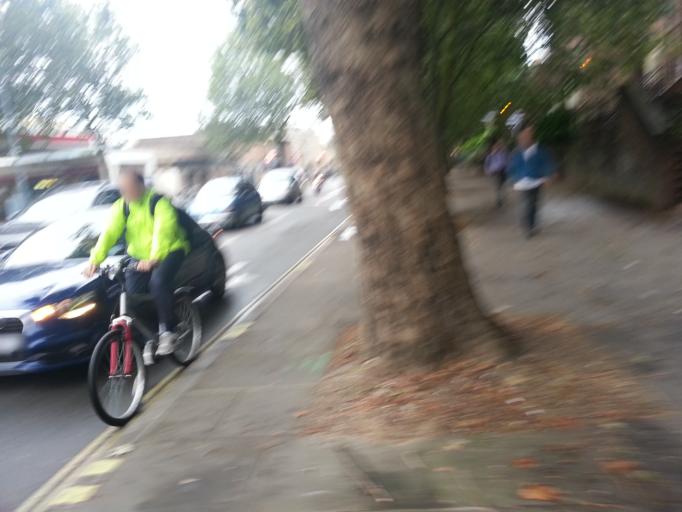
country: GB
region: England
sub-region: Greater London
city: Hammersmith
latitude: 51.5126
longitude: -0.2252
